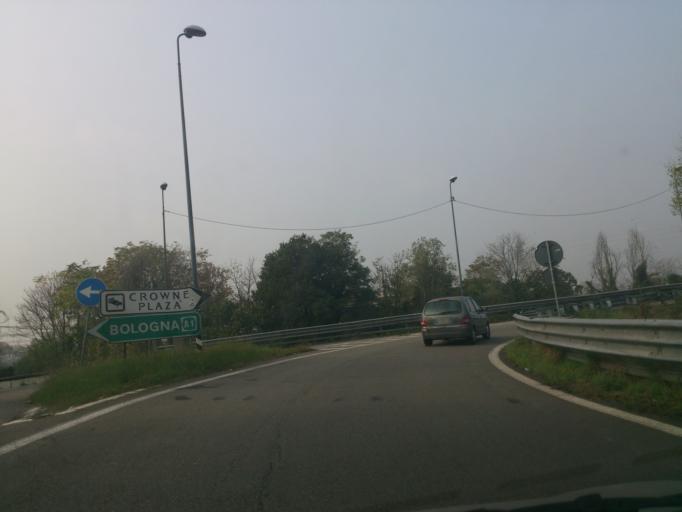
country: IT
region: Lombardy
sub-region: Citta metropolitana di Milano
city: Chiaravalle
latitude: 45.4220
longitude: 9.2504
